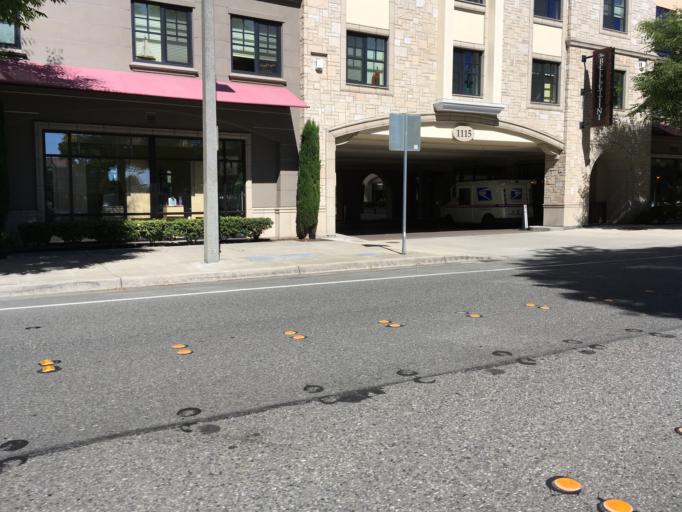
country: US
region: Washington
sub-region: King County
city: Bellevue
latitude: 47.6204
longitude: -122.1963
